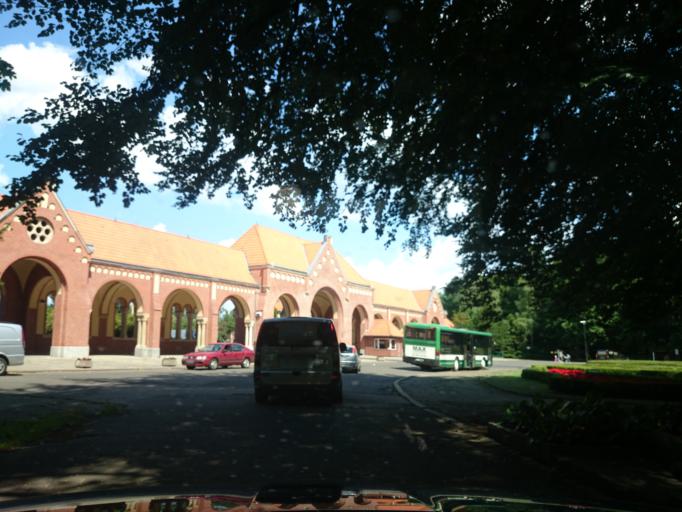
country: PL
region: West Pomeranian Voivodeship
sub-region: Szczecin
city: Szczecin
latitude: 53.4199
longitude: 14.5229
